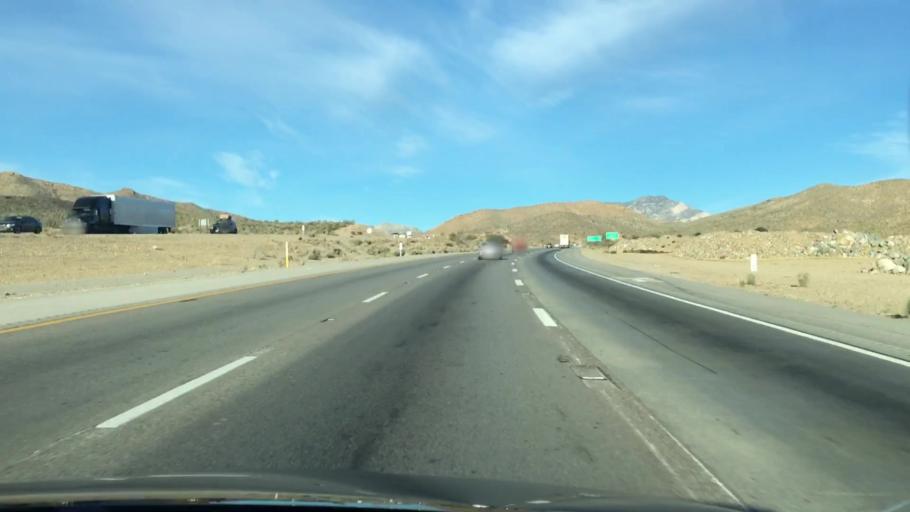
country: US
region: Nevada
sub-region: Clark County
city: Sandy Valley
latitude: 35.4627
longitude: -115.4779
